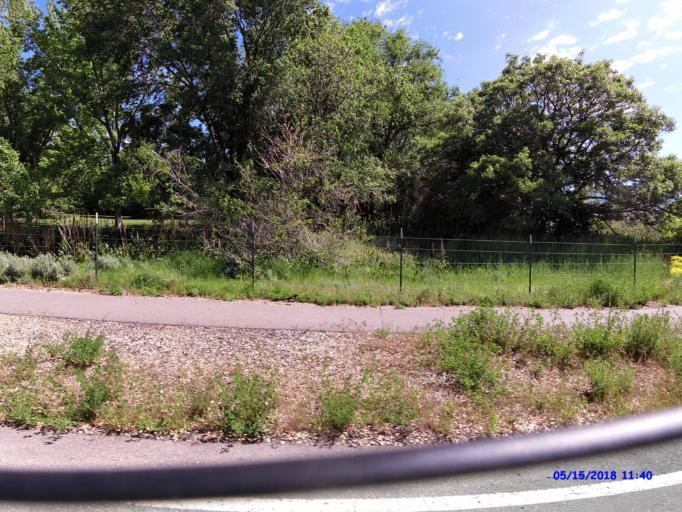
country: US
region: Utah
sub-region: Weber County
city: Washington Terrace
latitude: 41.1726
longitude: -111.9456
